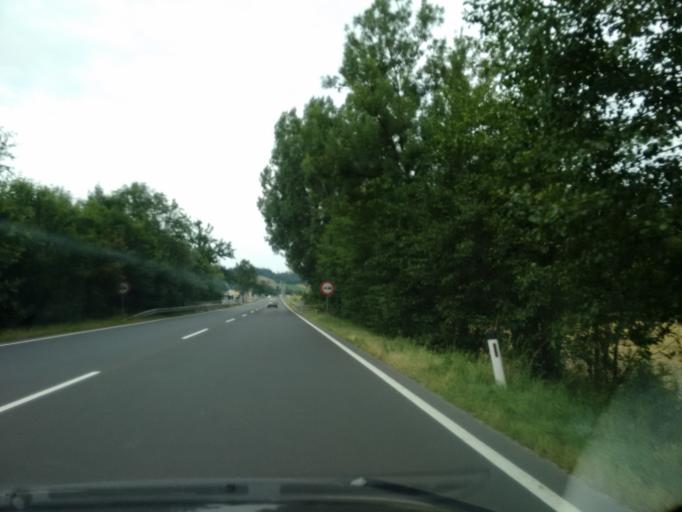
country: AT
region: Upper Austria
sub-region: Politischer Bezirk Grieskirchen
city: Bad Schallerbach
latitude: 48.2011
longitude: 13.9277
